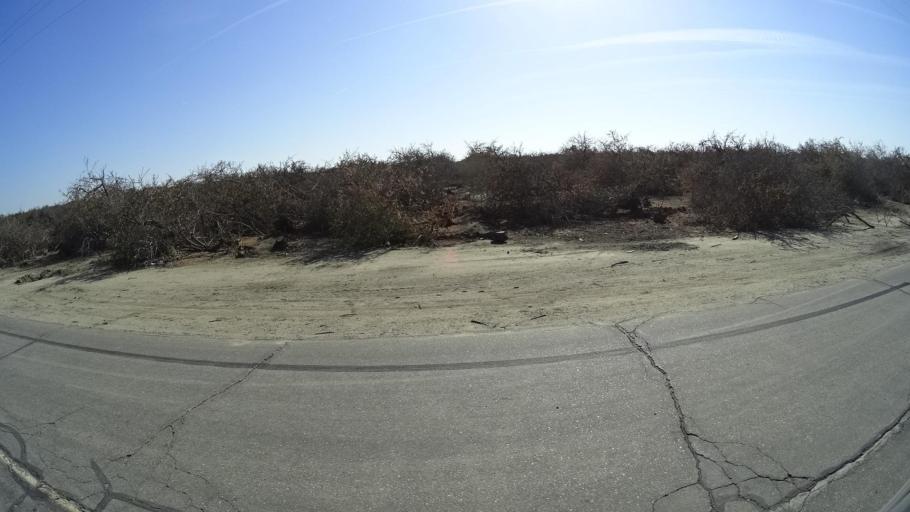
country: US
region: California
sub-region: Kern County
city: Wasco
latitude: 35.6669
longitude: -119.3461
